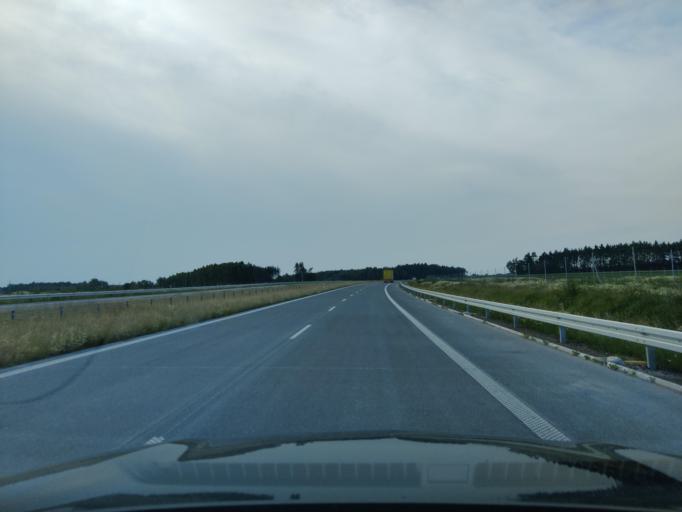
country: PL
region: Masovian Voivodeship
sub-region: Powiat mlawski
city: Strzegowo
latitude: 52.8851
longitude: 20.2662
